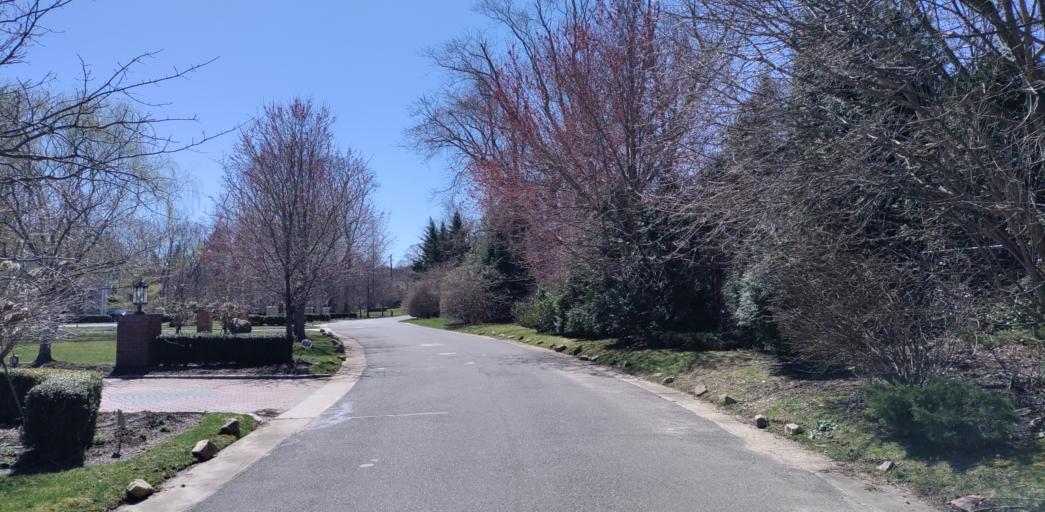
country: US
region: New York
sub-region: Nassau County
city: Greenvale
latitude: 40.8141
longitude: -73.6180
